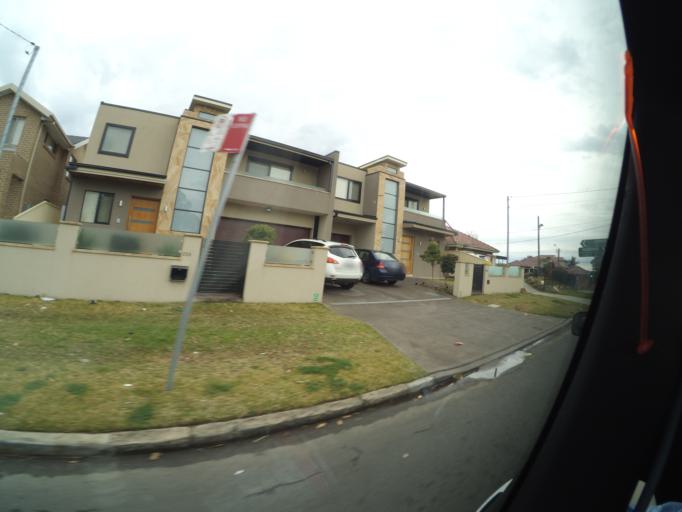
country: AU
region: New South Wales
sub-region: Bankstown
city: Bankstown
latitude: -33.9078
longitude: 151.0204
